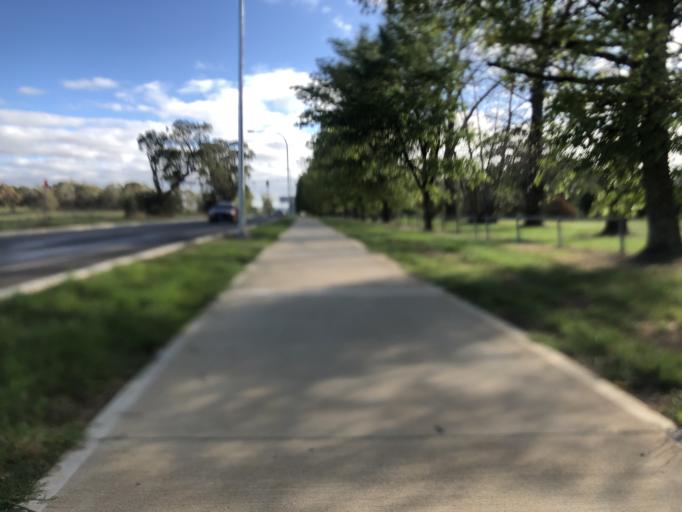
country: AU
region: New South Wales
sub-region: Orange Municipality
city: Orange
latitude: -33.3150
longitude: 149.0925
